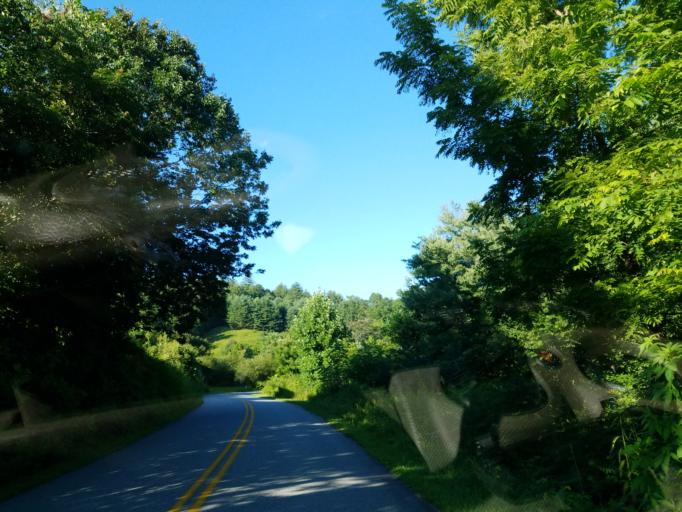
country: US
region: Georgia
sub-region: Union County
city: Blairsville
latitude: 34.7636
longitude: -84.1018
